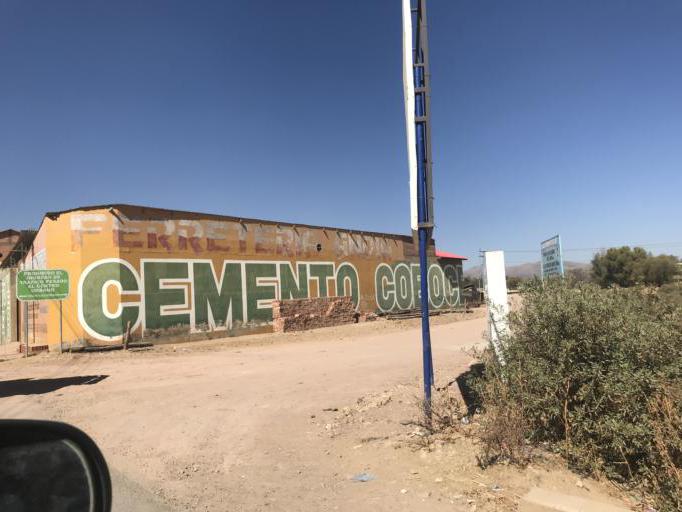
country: BO
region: Cochabamba
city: Cliza
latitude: -17.5936
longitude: -65.9383
